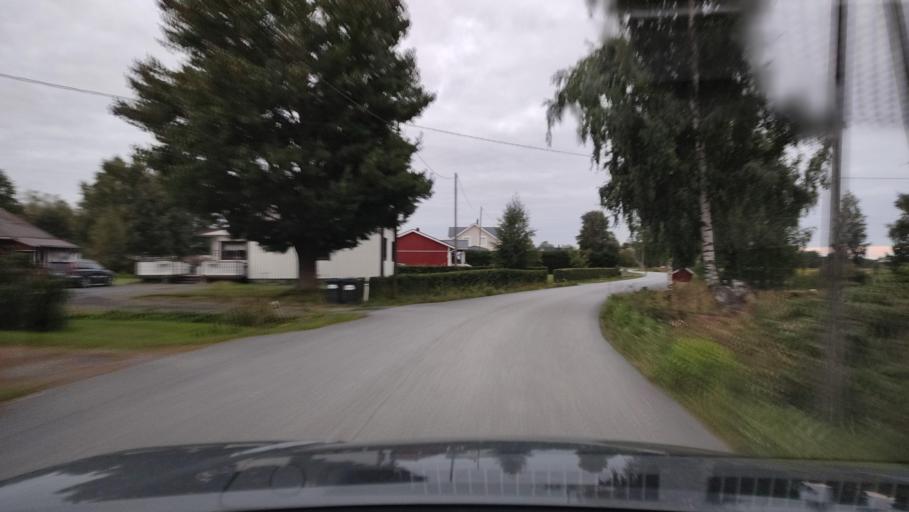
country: FI
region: Ostrobothnia
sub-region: Sydosterbotten
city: Kristinestad
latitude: 62.2479
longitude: 21.5064
